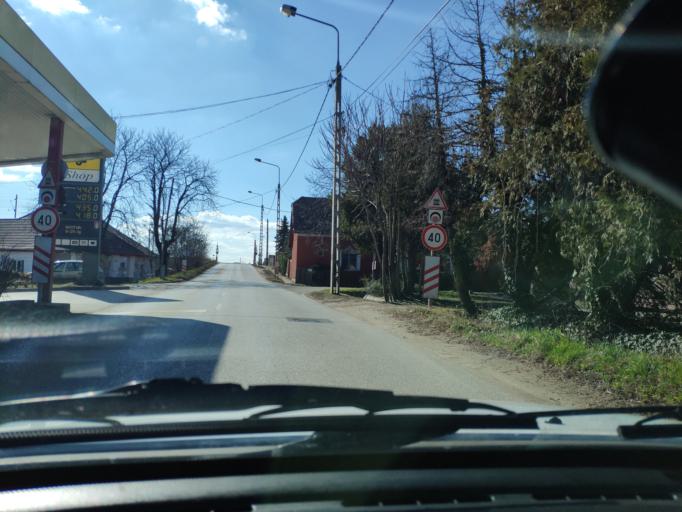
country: HU
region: Pest
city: Ecser
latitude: 47.4402
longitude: 19.3195
